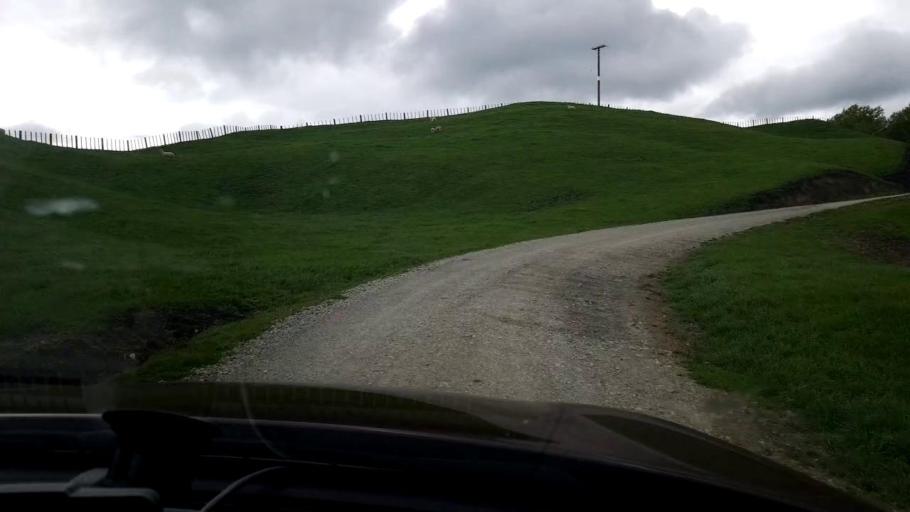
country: NZ
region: Gisborne
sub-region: Gisborne District
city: Gisborne
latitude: -38.3677
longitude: 177.9646
